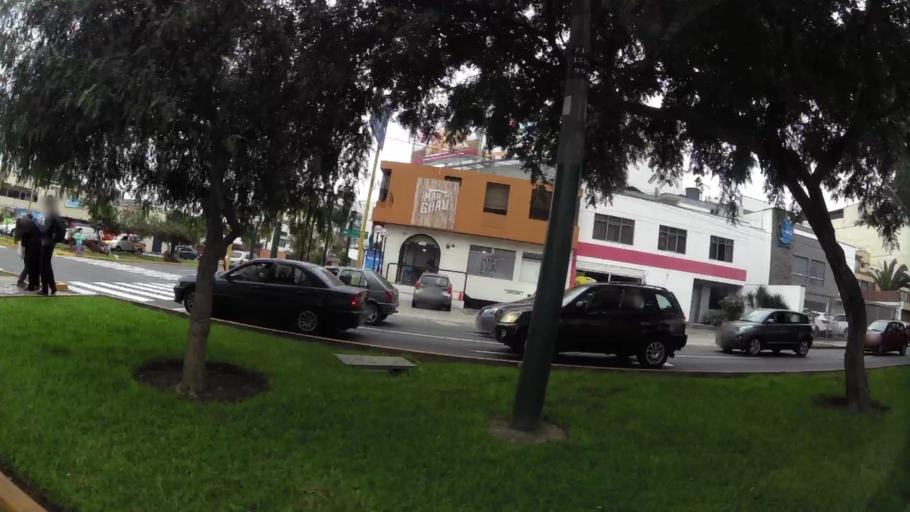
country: PE
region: Lima
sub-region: Lima
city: Surco
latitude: -12.1238
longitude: -76.9902
